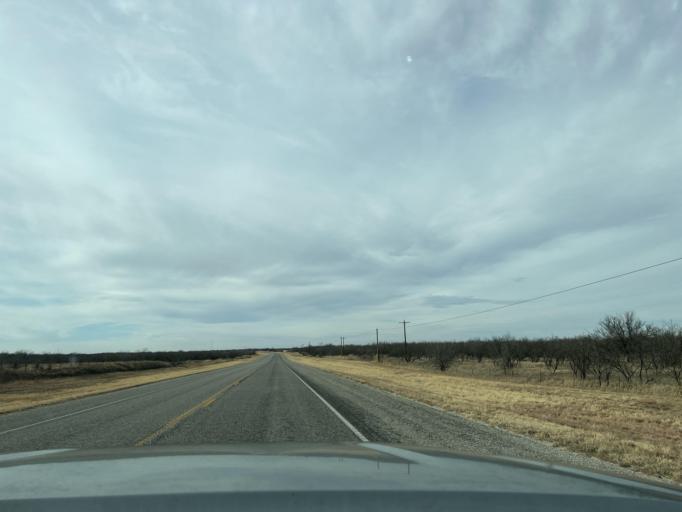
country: US
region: Texas
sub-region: Shackelford County
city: Albany
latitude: 32.7612
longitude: -99.5720
